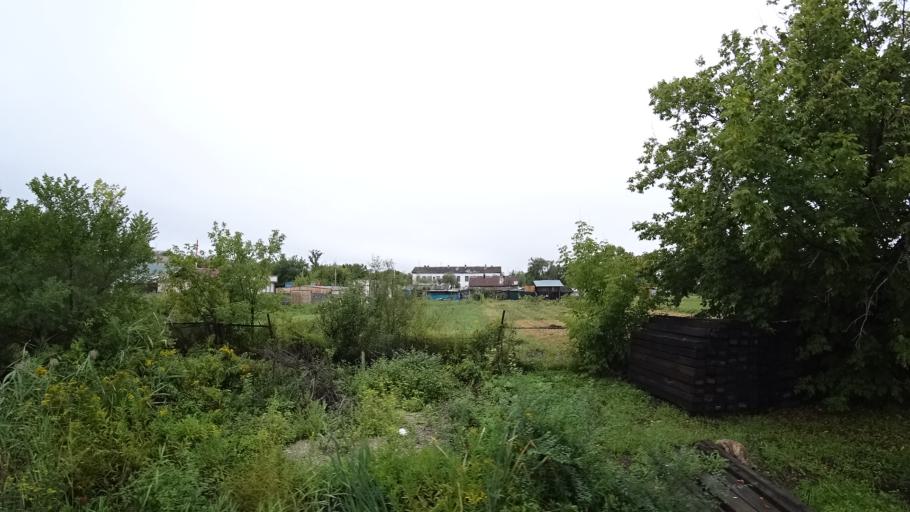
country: RU
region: Primorskiy
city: Monastyrishche
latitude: 44.2001
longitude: 132.4277
